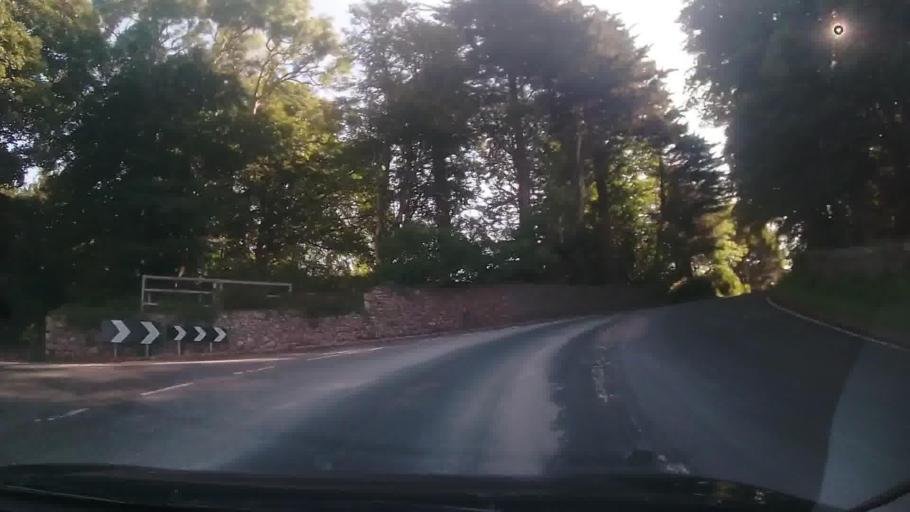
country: GB
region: England
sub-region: Cumbria
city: Seascale
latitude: 54.3584
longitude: -3.3860
